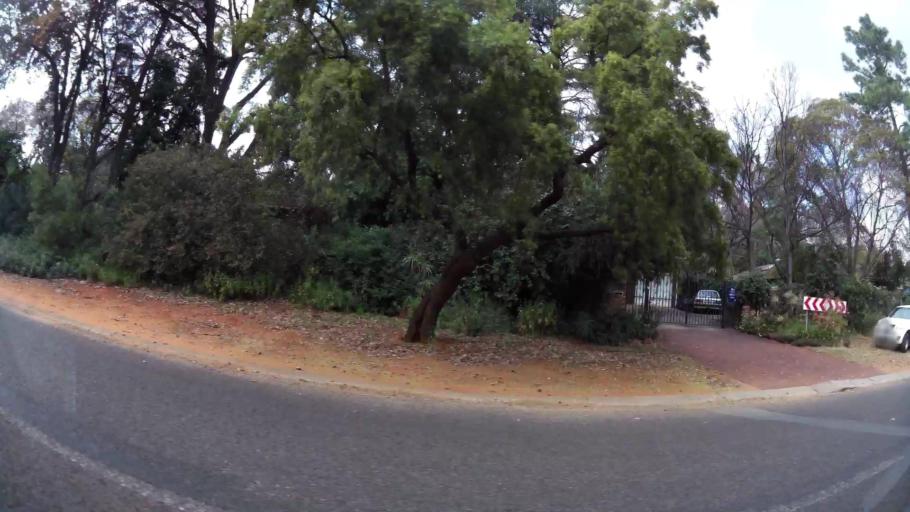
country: ZA
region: Gauteng
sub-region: City of Tshwane Metropolitan Municipality
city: Pretoria
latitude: -25.7553
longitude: 28.2956
